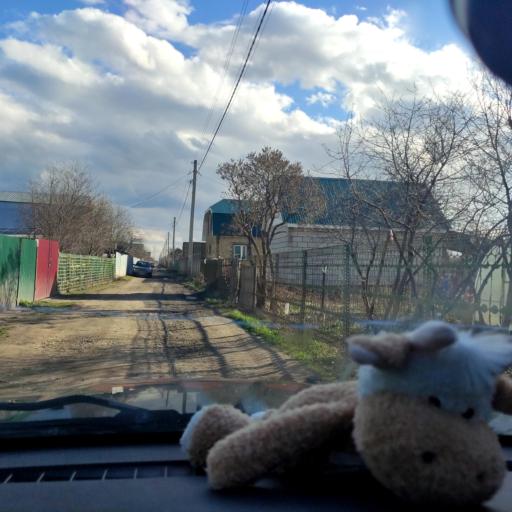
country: RU
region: Samara
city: Tol'yatti
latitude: 53.5971
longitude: 49.3092
